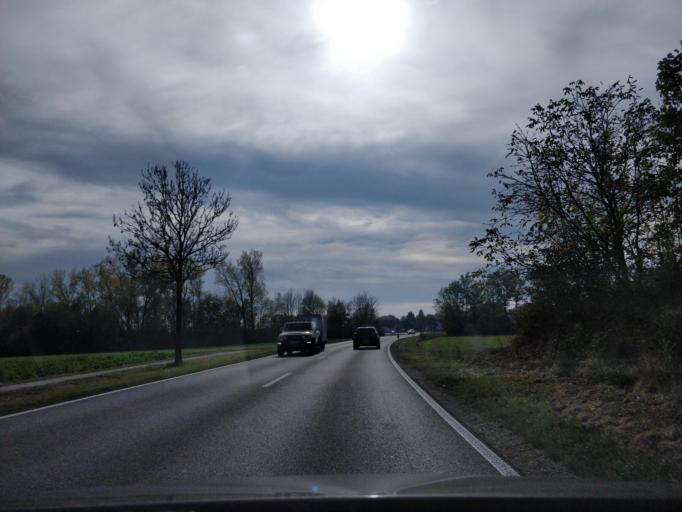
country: DE
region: Bavaria
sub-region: Swabia
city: Konigsbrunn
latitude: 48.2609
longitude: 10.9052
